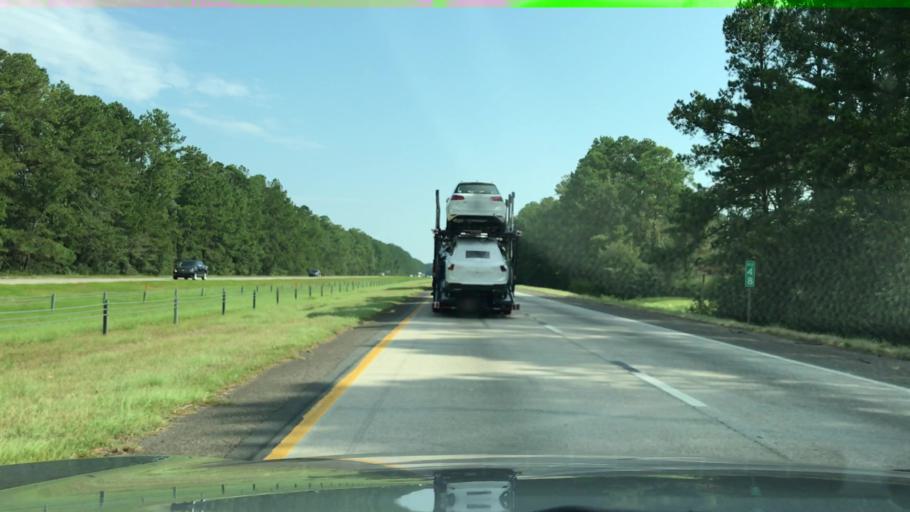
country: US
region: South Carolina
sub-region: Colleton County
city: Walterboro
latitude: 32.8114
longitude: -80.7648
